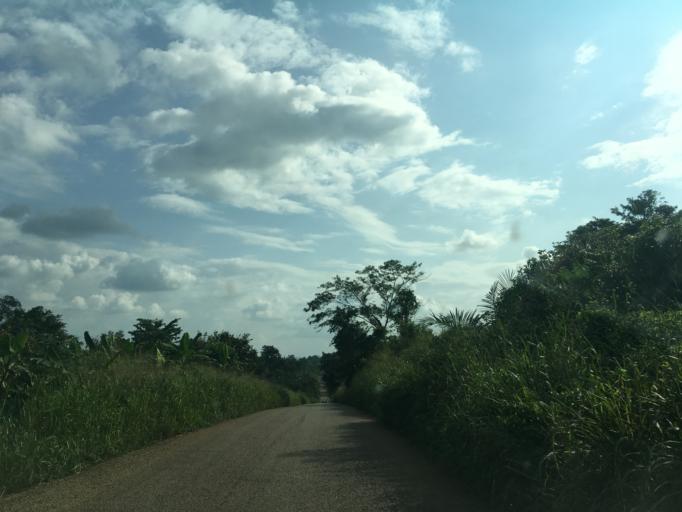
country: GH
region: Western
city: Bibiani
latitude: 6.7693
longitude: -2.5708
